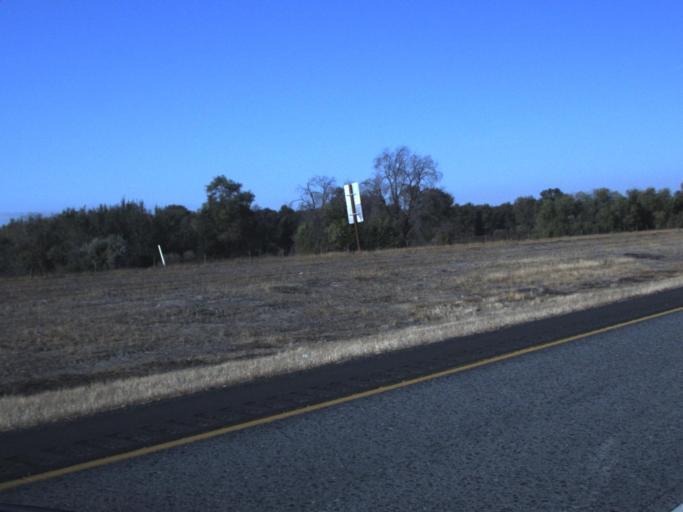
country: US
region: Washington
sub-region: Yakima County
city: Toppenish
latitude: 46.4130
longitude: -120.2978
